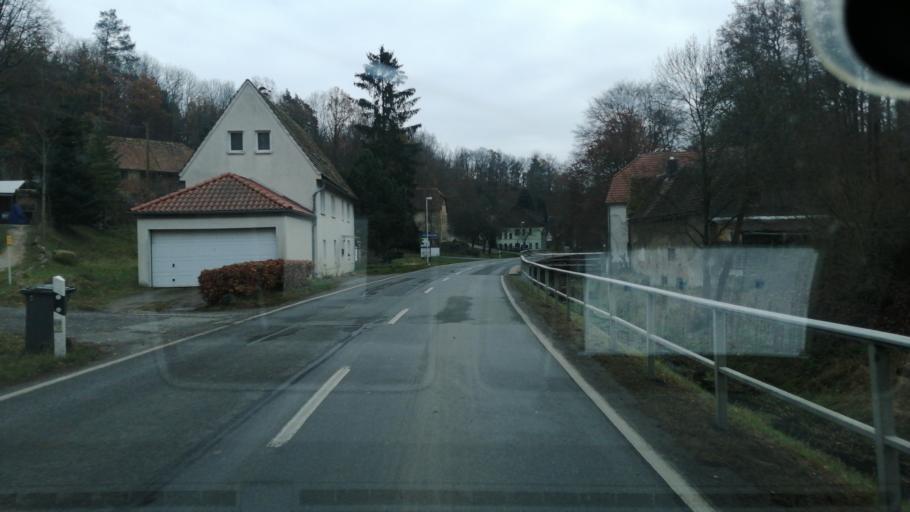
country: DE
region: Saxony
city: Bernstadt
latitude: 51.0616
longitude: 14.8074
